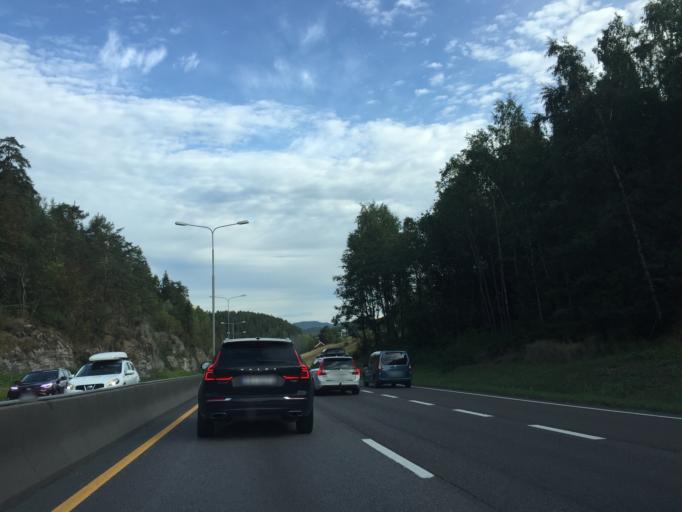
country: NO
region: Akershus
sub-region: Oppegard
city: Kolbotn
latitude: 59.8545
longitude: 10.8331
